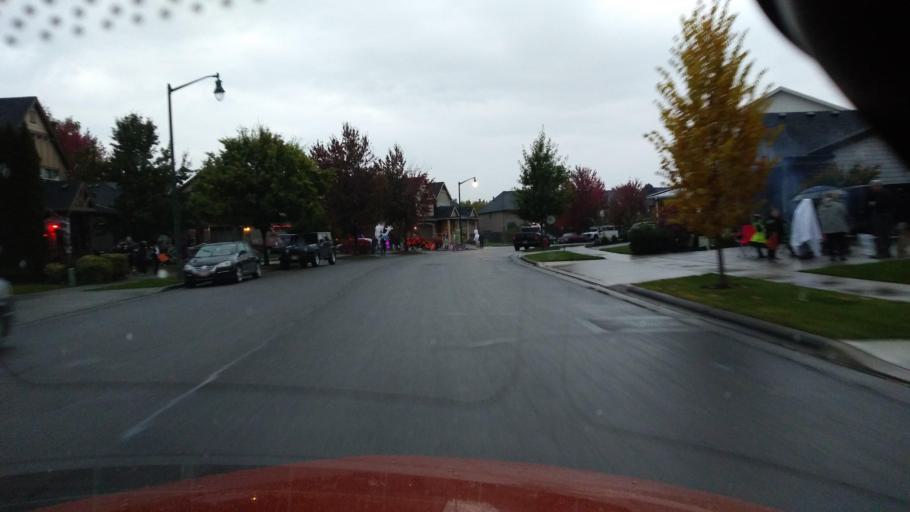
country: US
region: Oregon
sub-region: Washington County
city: Forest Grove
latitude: 45.5253
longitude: -123.1267
